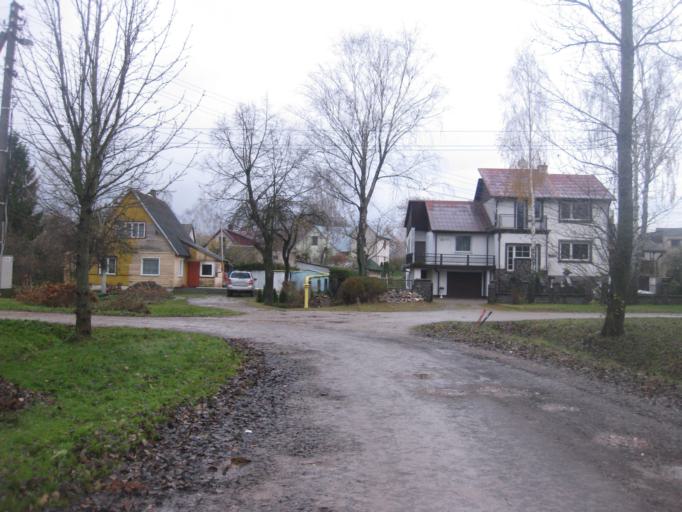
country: LT
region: Kauno apskritis
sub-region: Kaunas
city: Aleksotas
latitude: 54.8589
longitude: 23.8769
